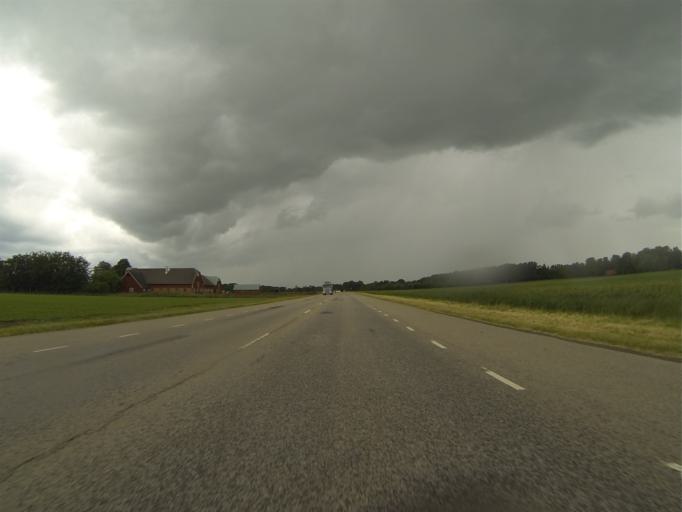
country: SE
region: Skane
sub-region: Hoors Kommun
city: Loberod
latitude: 55.7293
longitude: 13.4243
